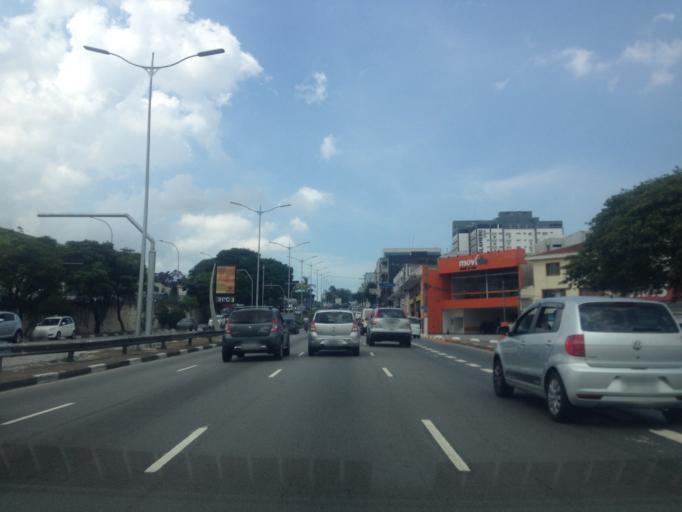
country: BR
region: Sao Paulo
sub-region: Sao Paulo
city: Sao Paulo
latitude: -23.6198
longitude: -46.6621
